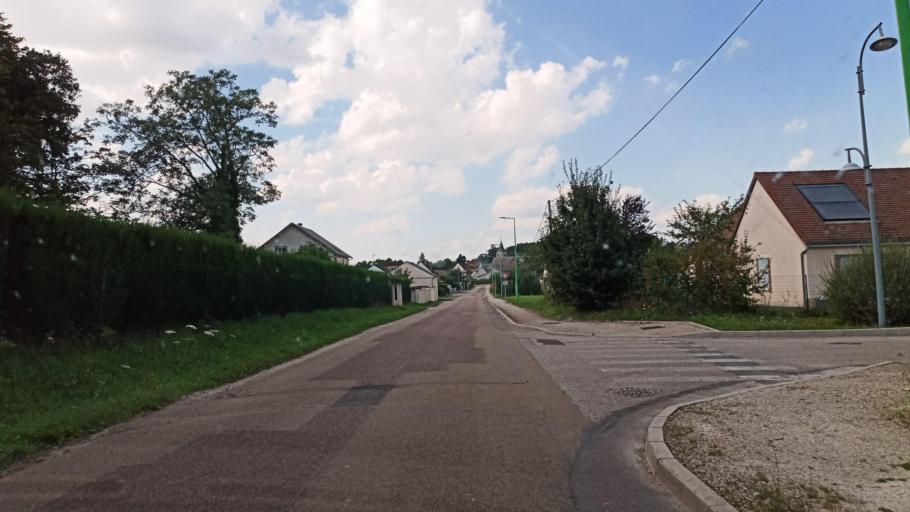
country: FR
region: Bourgogne
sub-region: Departement de l'Yonne
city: Saint-Valerien
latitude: 48.1748
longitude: 3.0979
